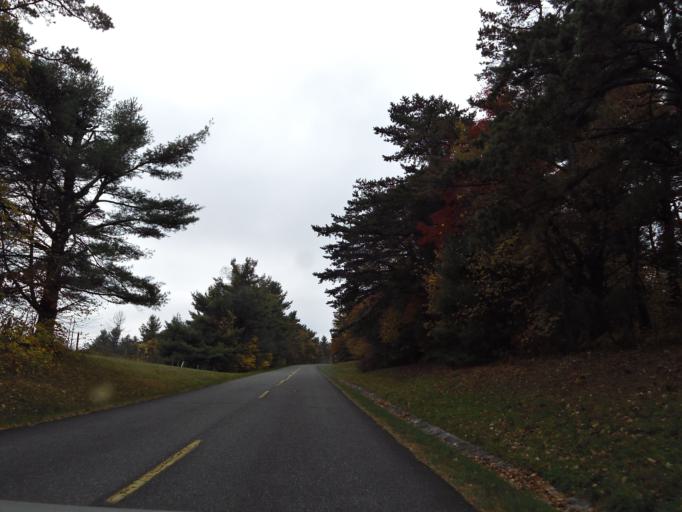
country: US
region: North Carolina
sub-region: Ashe County
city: West Jefferson
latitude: 36.2900
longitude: -81.4022
